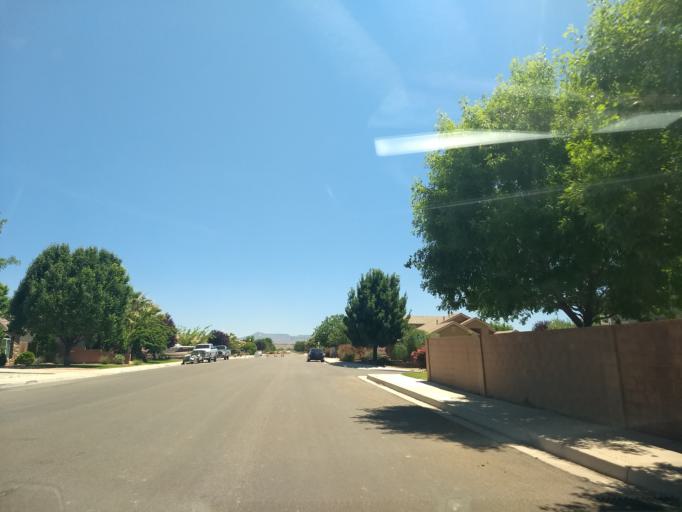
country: US
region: Utah
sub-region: Washington County
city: Washington
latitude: 37.0998
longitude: -113.5136
